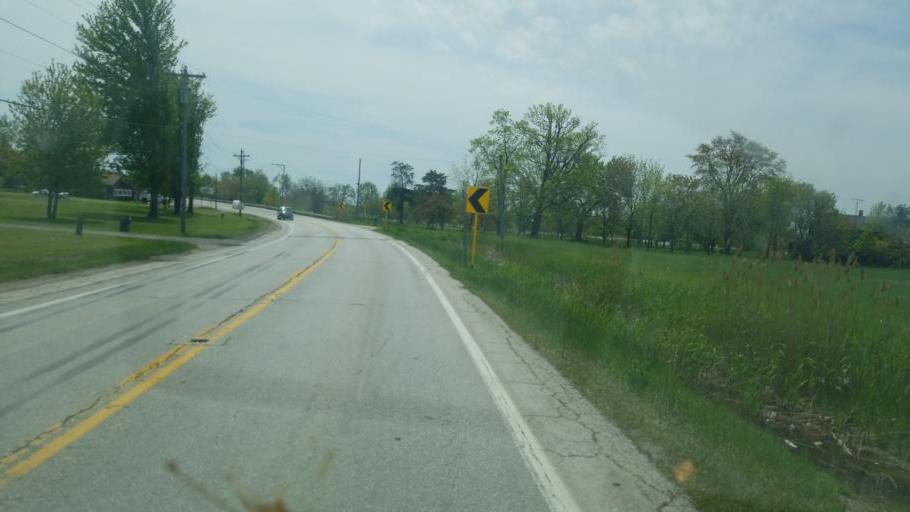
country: US
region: Ohio
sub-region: Ottawa County
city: Oak Harbor
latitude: 41.5877
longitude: -83.0966
